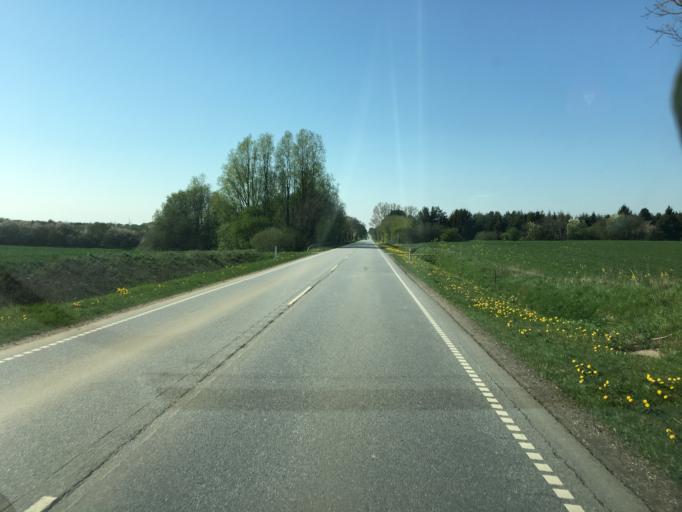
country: DK
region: South Denmark
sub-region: Haderslev Kommune
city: Vojens
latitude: 55.2969
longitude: 9.3802
